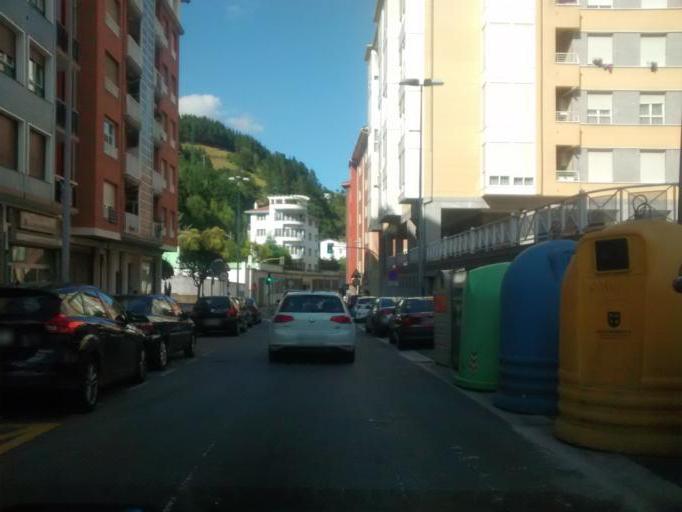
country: ES
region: Basque Country
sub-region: Provincia de Guipuzcoa
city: Eibar
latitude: 43.1882
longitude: -2.4605
